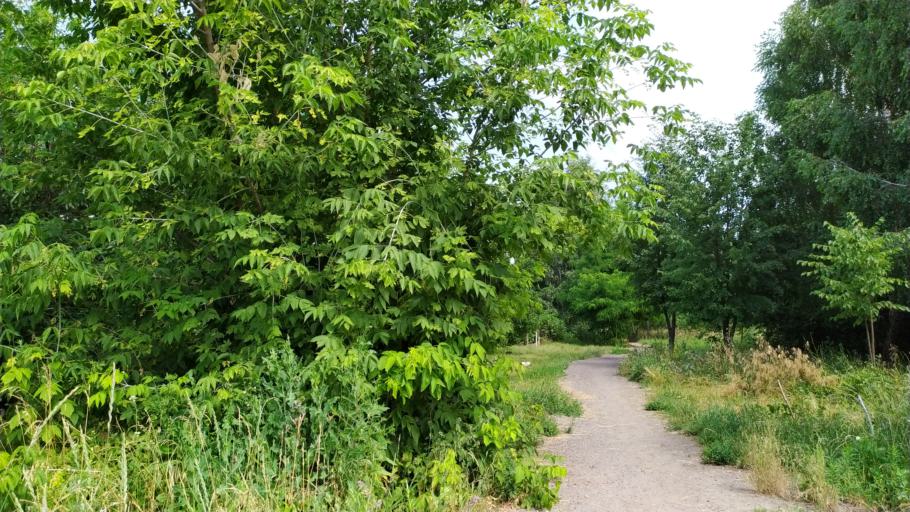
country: RU
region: Kursk
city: Kursk
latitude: 51.6433
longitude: 36.1360
